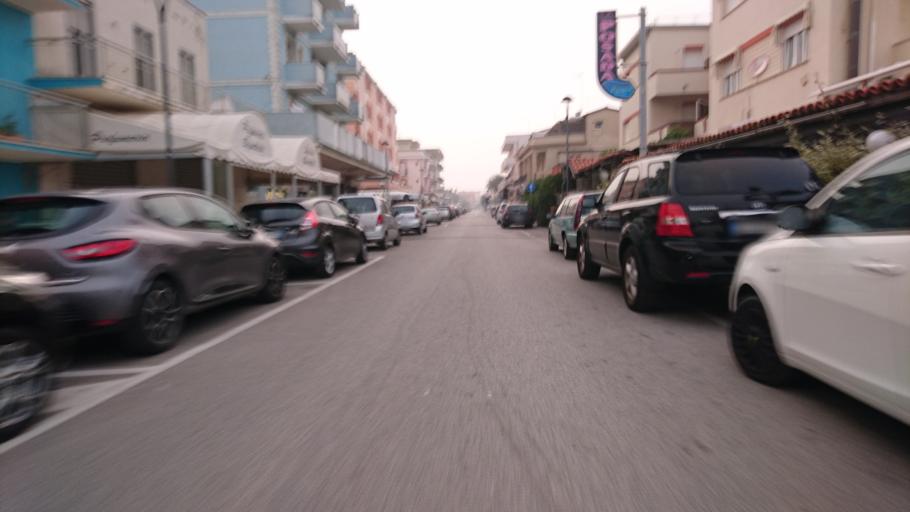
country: IT
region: Emilia-Romagna
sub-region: Provincia di Rimini
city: Rimini
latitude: 44.0767
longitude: 12.5575
